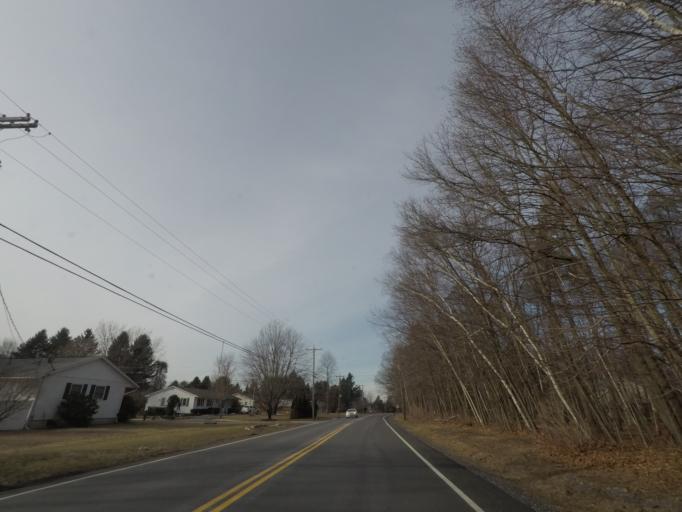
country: US
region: New York
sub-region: Columbia County
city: Valatie
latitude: 42.4034
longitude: -73.6725
